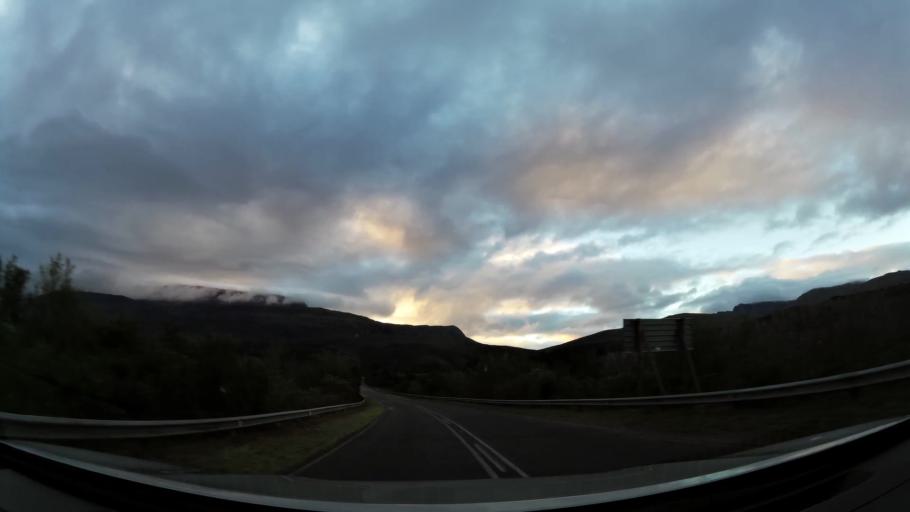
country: ZA
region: Western Cape
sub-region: Overberg District Municipality
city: Swellendam
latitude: -34.0067
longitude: 20.7080
